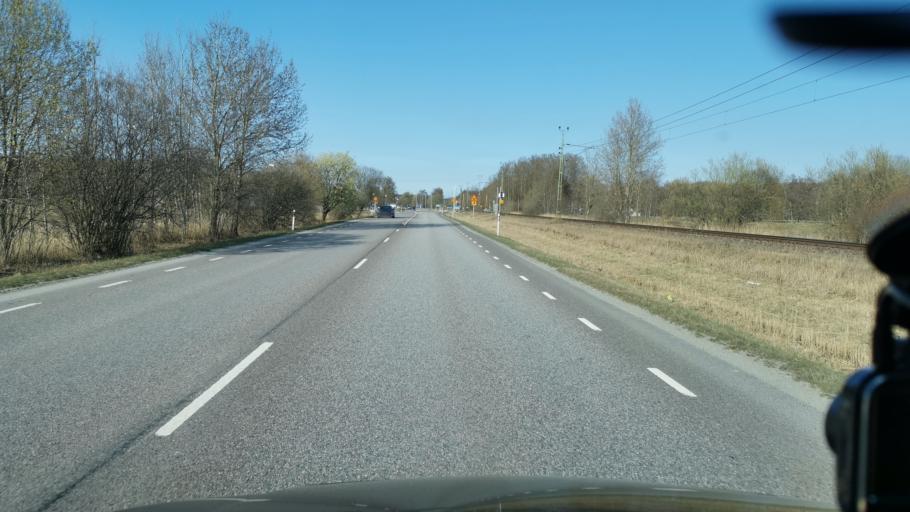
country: SE
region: Vaestra Goetaland
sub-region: Stenungsunds Kommun
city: Stora Hoga
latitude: 58.0059
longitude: 11.8291
